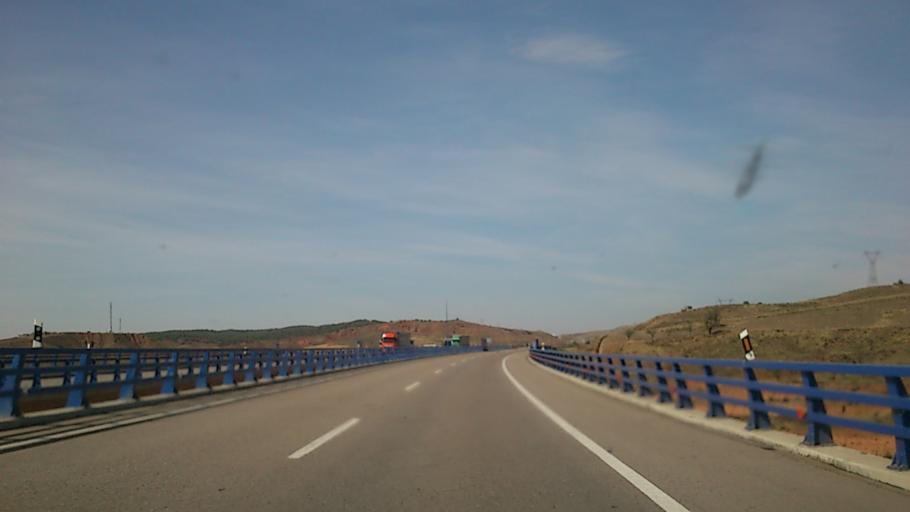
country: ES
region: Aragon
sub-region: Provincia de Teruel
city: Calamocha
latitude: 40.9465
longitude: -1.2737
